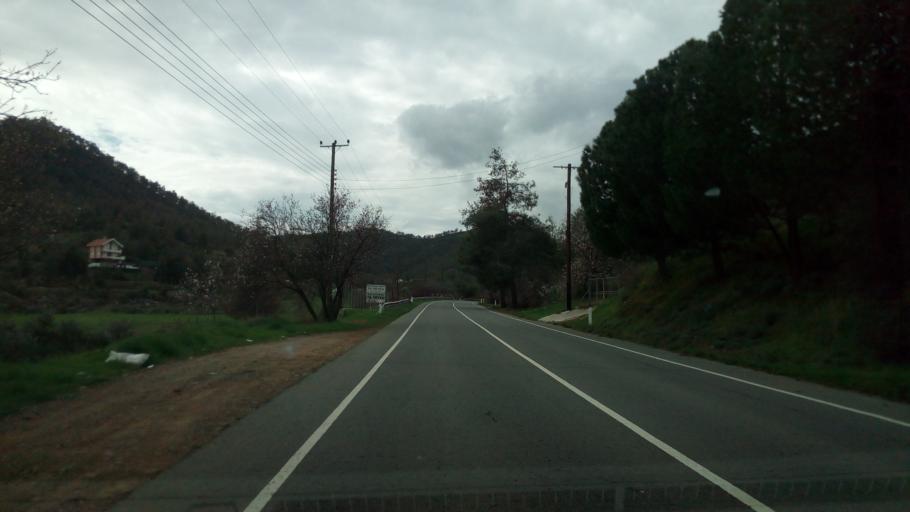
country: CY
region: Lefkosia
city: Klirou
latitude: 35.0017
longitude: 33.1426
